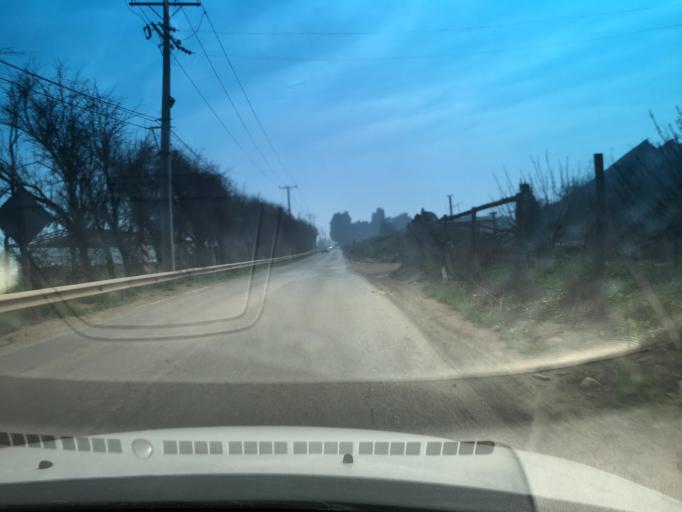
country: CL
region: Santiago Metropolitan
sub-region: Provincia de Chacabuco
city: Lampa
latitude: -33.3572
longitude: -70.8038
